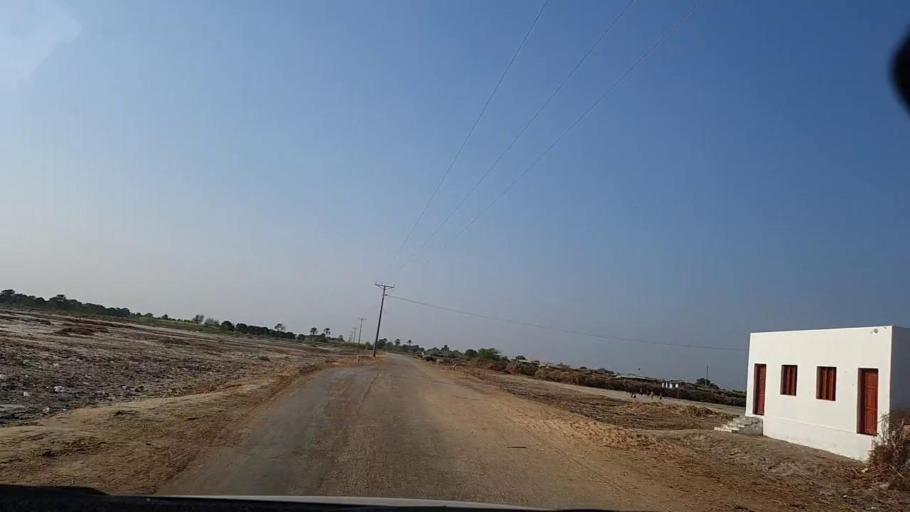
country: PK
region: Sindh
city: Mirwah Gorchani
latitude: 25.2172
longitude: 68.9929
